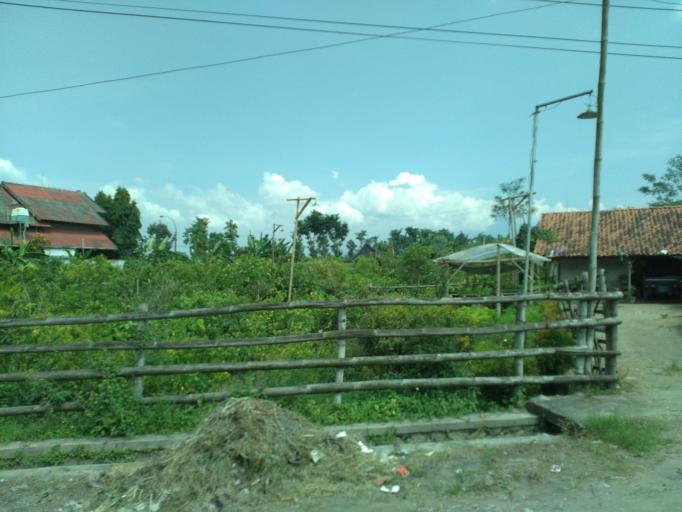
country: ID
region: Central Java
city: Candi Prambanan
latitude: -7.7498
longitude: 110.5210
